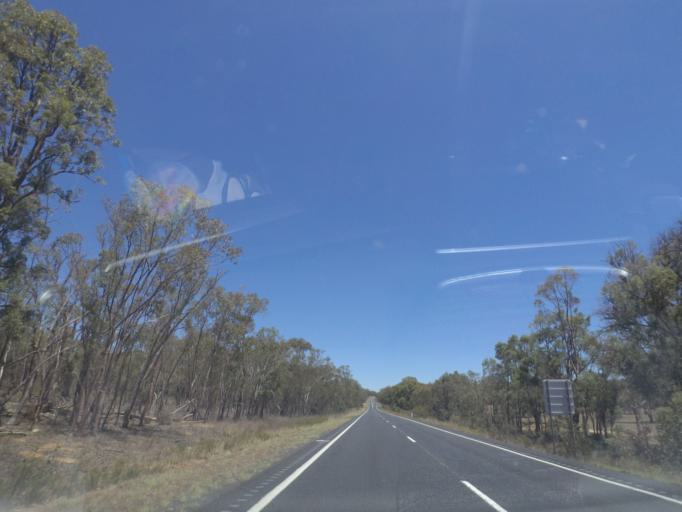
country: AU
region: New South Wales
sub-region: Warrumbungle Shire
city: Coonabarabran
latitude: -31.2219
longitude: 149.3244
